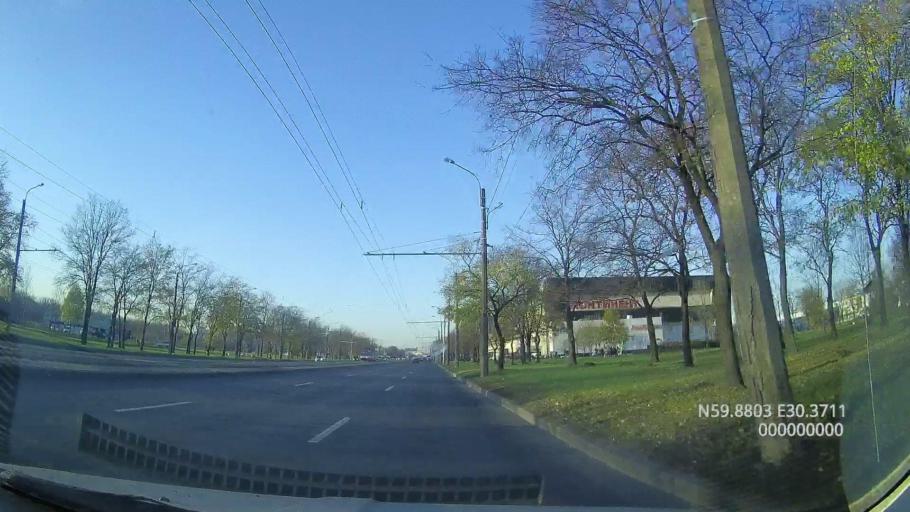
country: RU
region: St.-Petersburg
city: Kupchino
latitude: 59.8804
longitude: 30.3715
